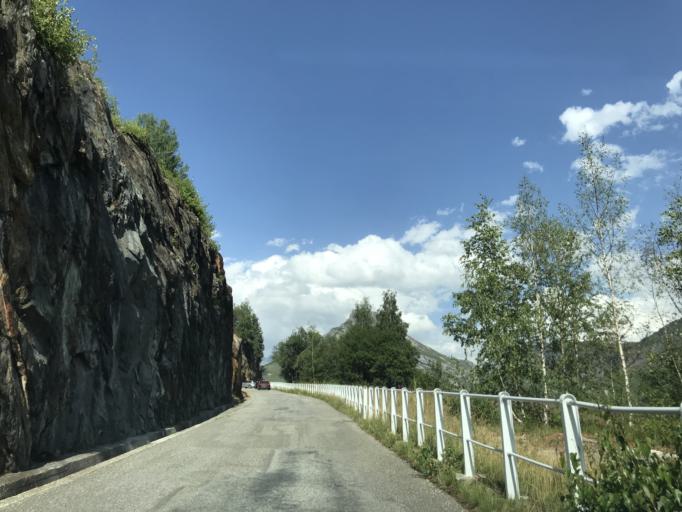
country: FR
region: Rhone-Alpes
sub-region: Departement de la Savoie
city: Beaufort
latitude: 45.6880
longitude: 6.6250
